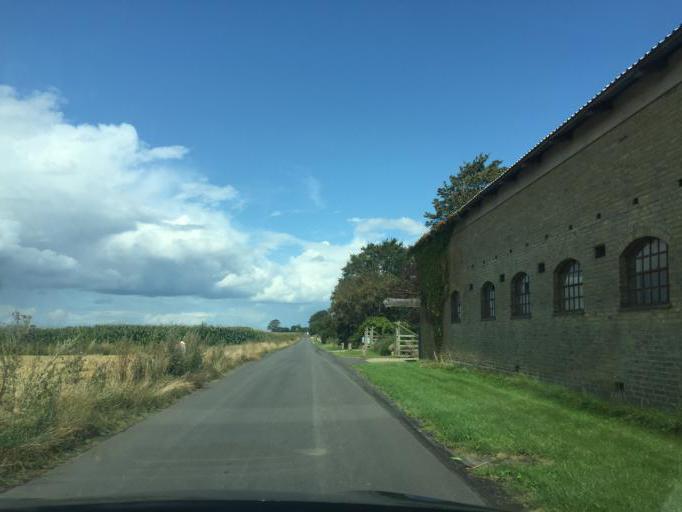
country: DK
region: South Denmark
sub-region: Faaborg-Midtfyn Kommune
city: Arslev
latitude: 55.3309
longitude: 10.4838
